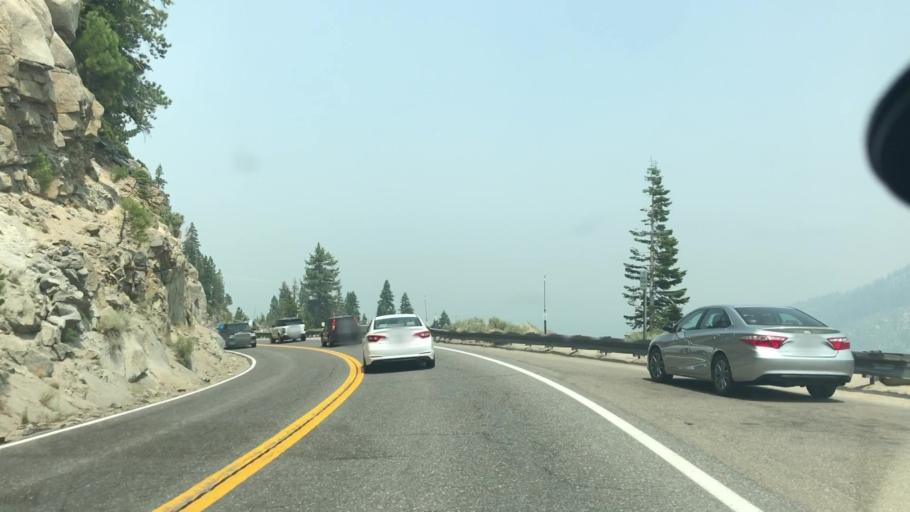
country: US
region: California
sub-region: El Dorado County
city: South Lake Tahoe
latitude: 38.8226
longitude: -120.0280
